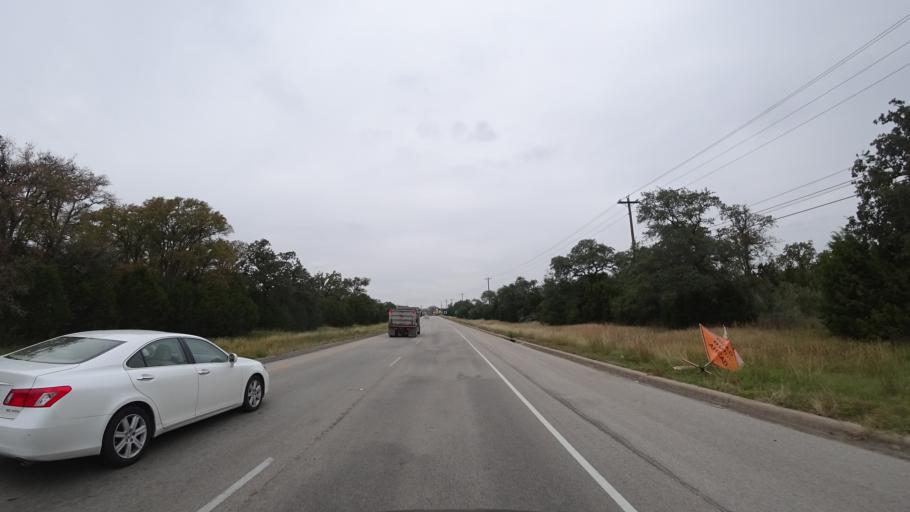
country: US
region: Texas
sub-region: Travis County
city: Shady Hollow
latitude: 30.1917
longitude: -97.9214
